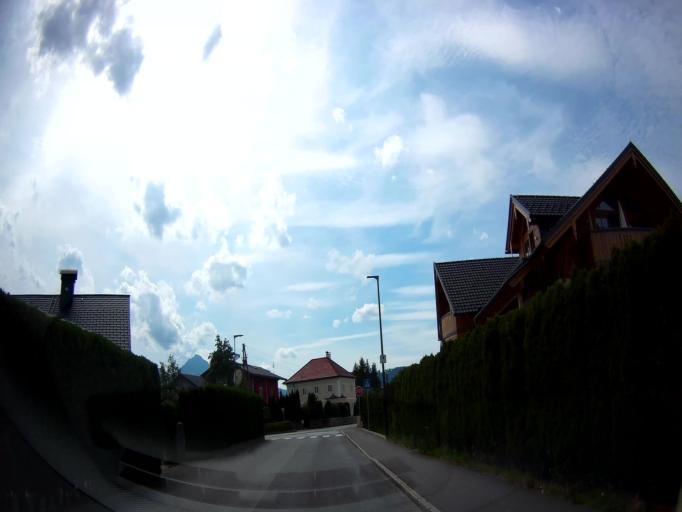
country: DE
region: Bavaria
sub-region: Upper Bavaria
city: Ainring
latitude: 47.7893
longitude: 12.9713
